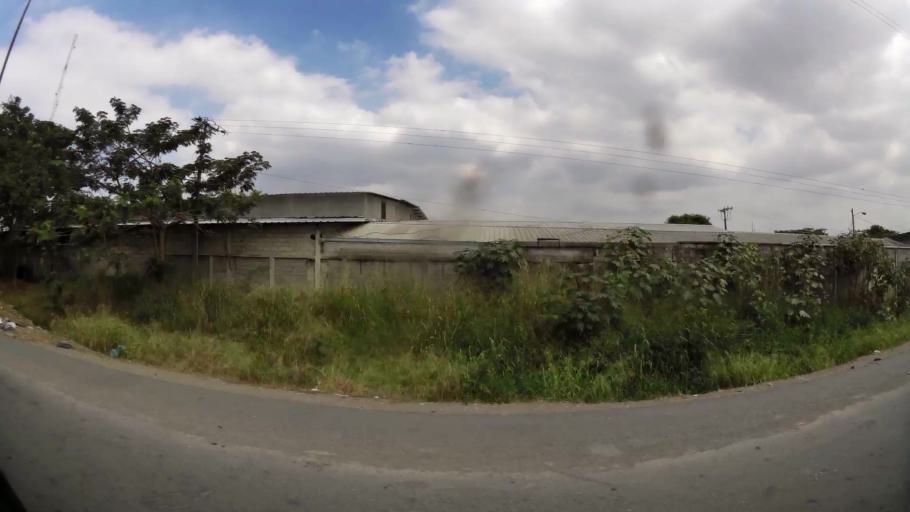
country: EC
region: Guayas
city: Santa Lucia
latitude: -2.0846
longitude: -79.9396
